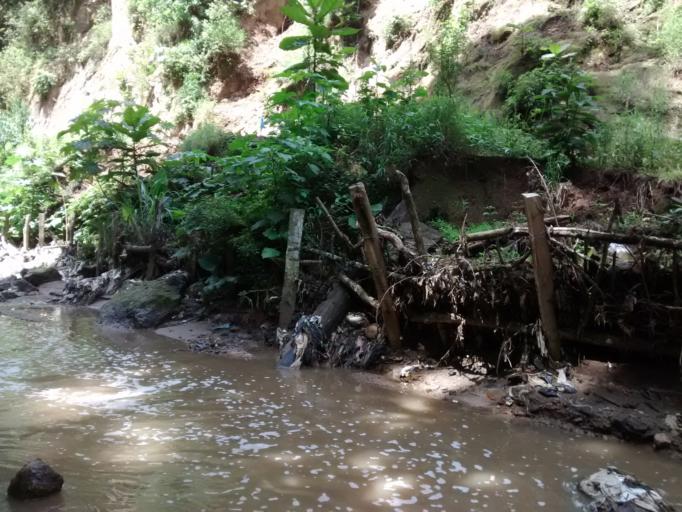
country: GT
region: Sacatepequez
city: Santo Domingo Xenacoj
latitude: 14.6953
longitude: -90.7254
